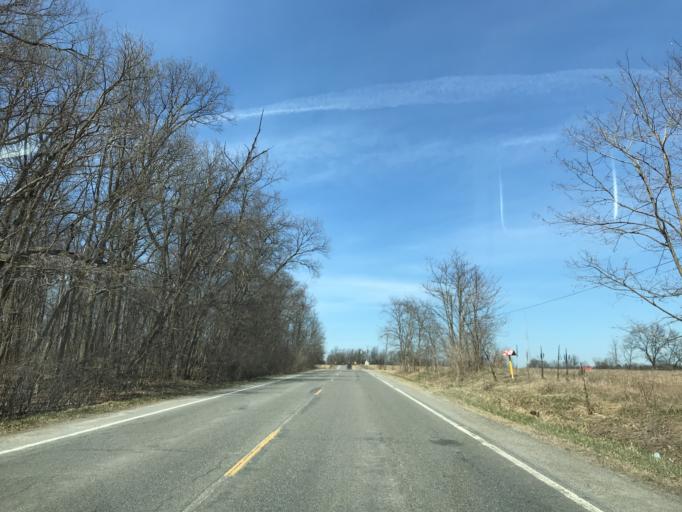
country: US
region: Michigan
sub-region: Washtenaw County
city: Ann Arbor
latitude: 42.3374
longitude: -83.7084
